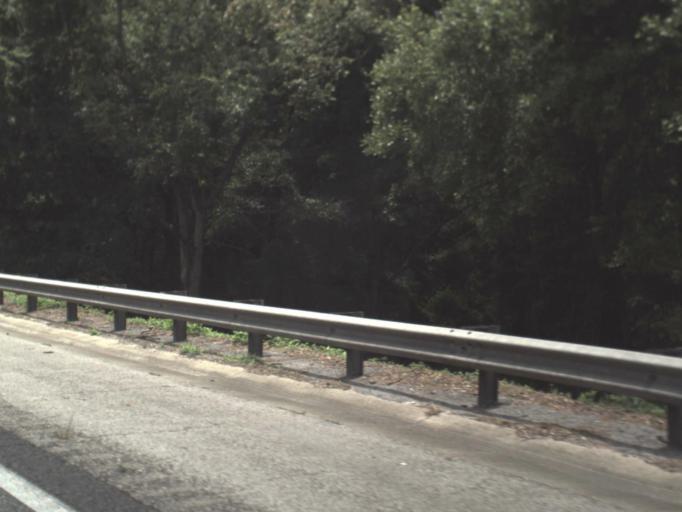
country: US
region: Florida
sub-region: Alachua County
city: Alachua
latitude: 29.7769
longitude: -82.5103
